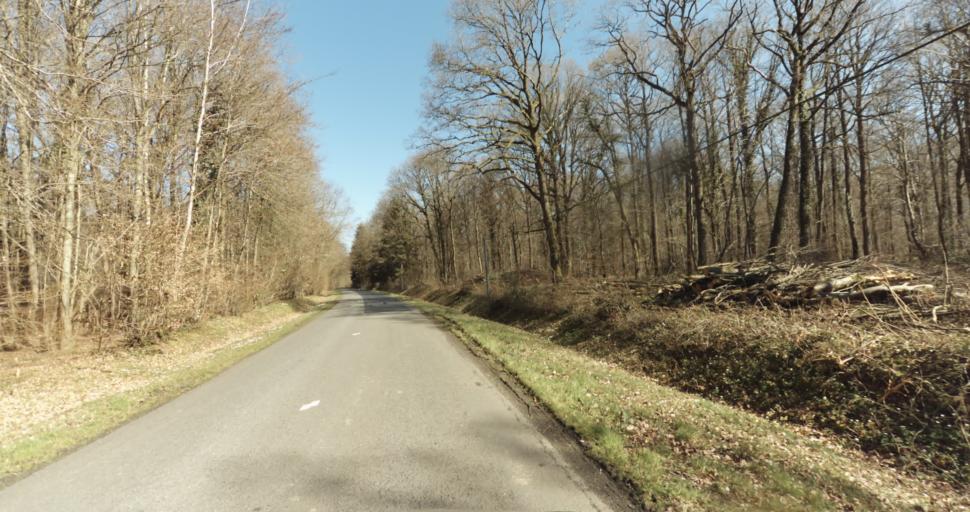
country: FR
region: Lower Normandy
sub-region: Departement de l'Orne
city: Trun
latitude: 48.9290
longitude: 0.0685
